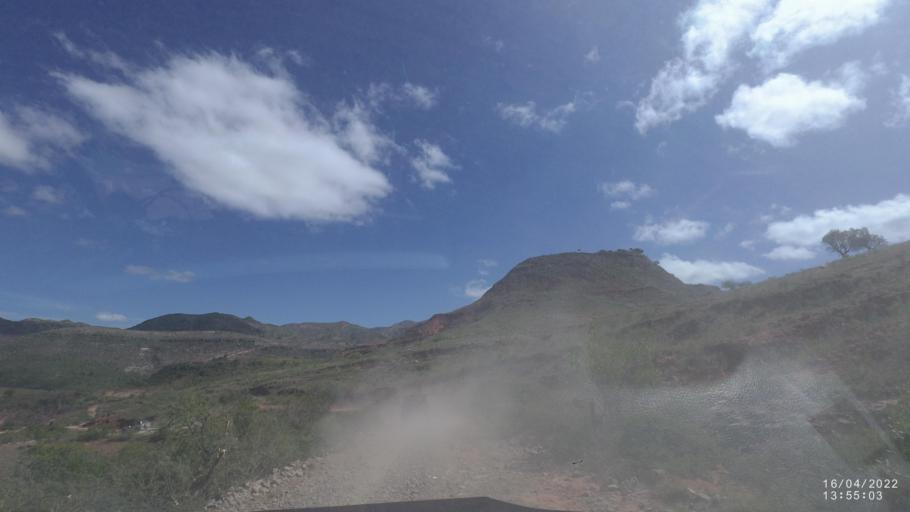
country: BO
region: Cochabamba
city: Mizque
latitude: -18.0273
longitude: -65.5640
